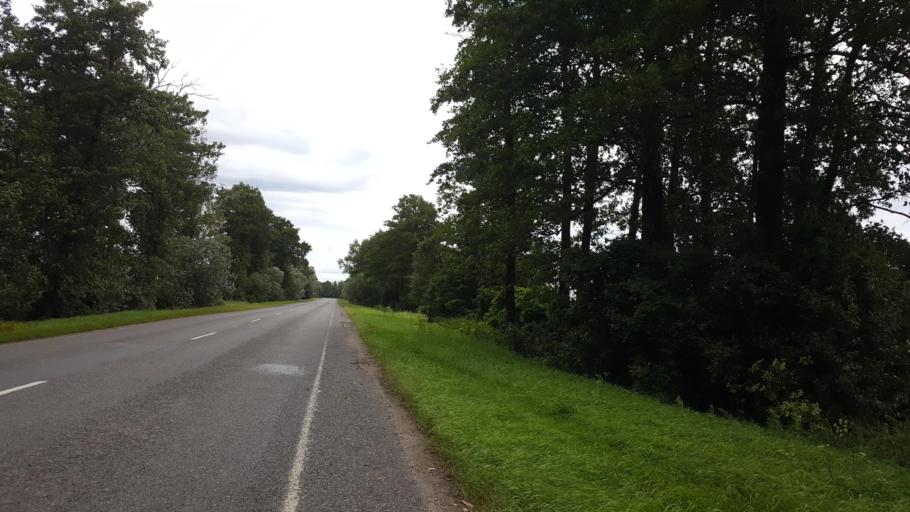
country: BY
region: Brest
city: Zhabinka
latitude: 52.2938
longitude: 23.9390
